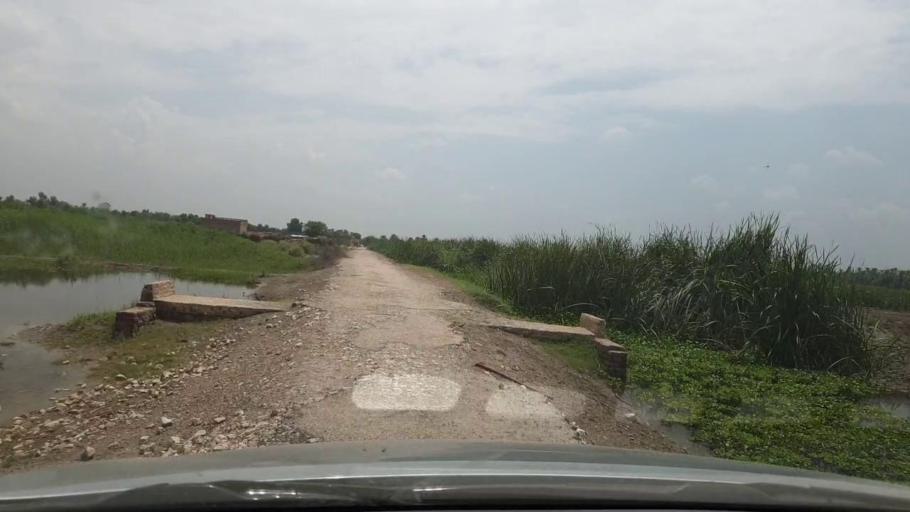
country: PK
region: Sindh
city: Kot Diji
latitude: 27.4241
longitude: 68.7611
